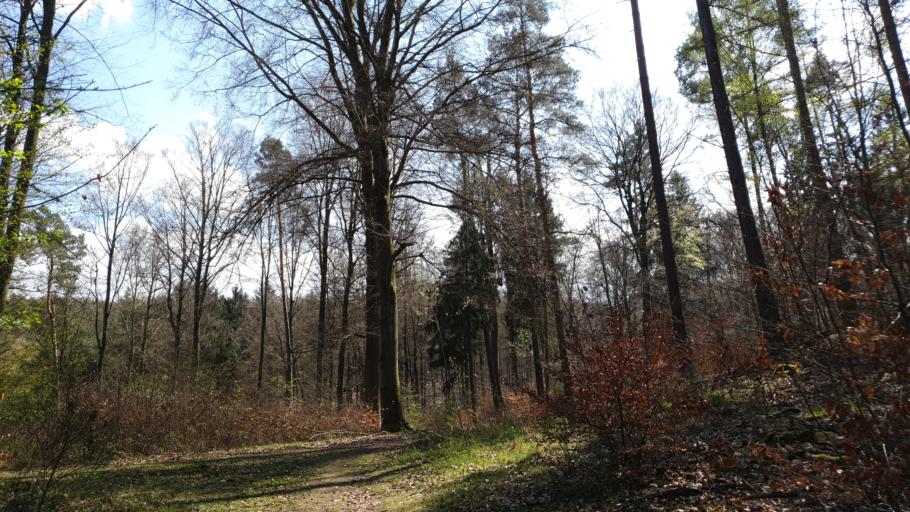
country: DE
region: Rheinland-Pfalz
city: Kaiserslautern
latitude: 49.4369
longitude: 7.7896
